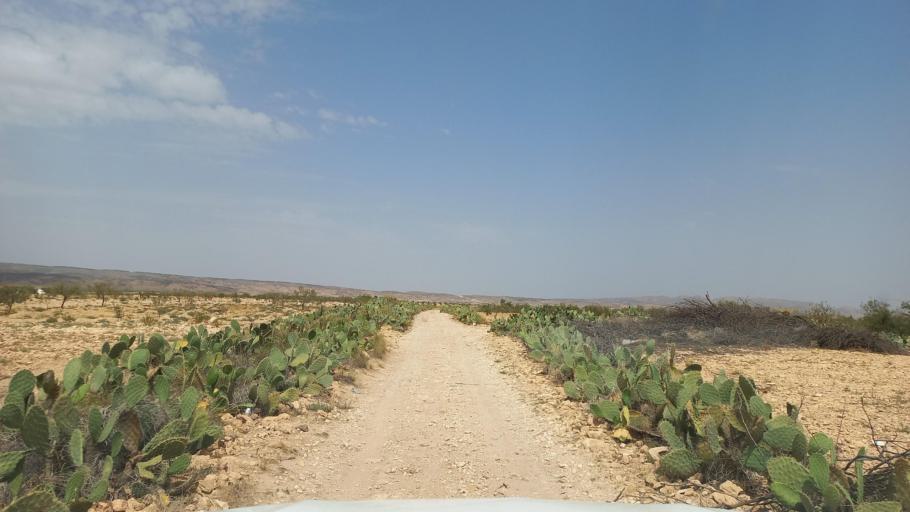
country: TN
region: Al Qasrayn
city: Kasserine
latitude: 35.2885
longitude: 9.0056
